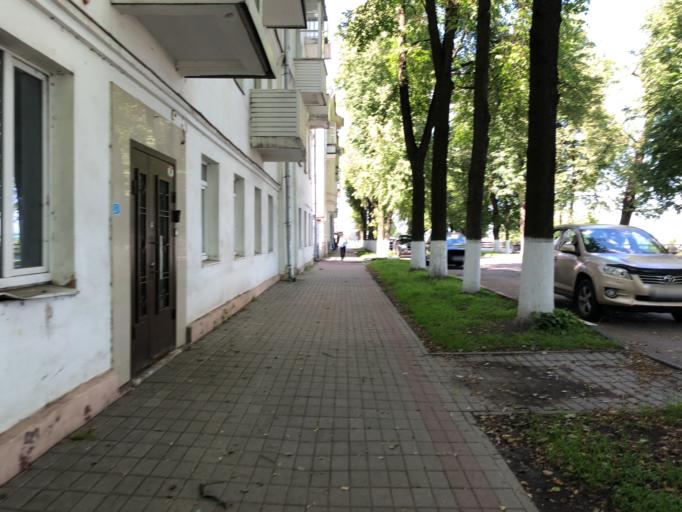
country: RU
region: Jaroslavl
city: Yaroslavl
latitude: 57.6316
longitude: 39.8942
